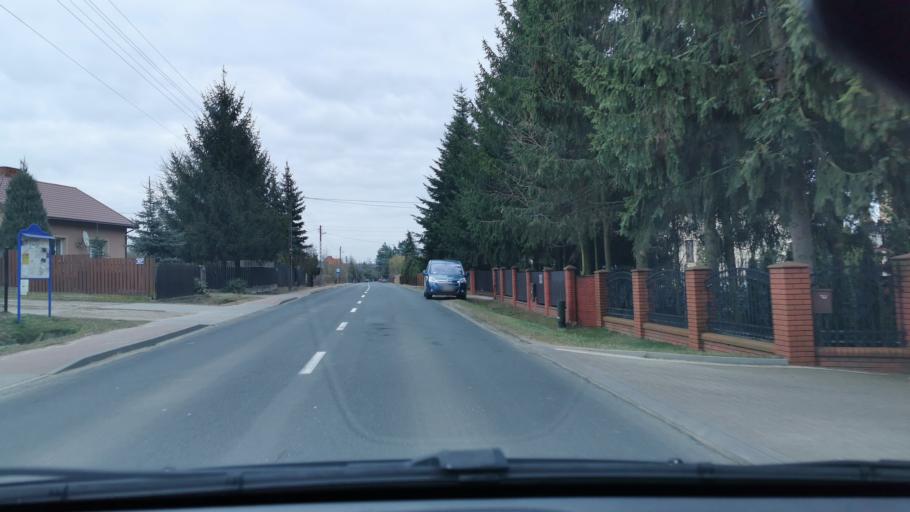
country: PL
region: Masovian Voivodeship
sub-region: Powiat zyrardowski
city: Radziejowice
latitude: 52.0097
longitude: 20.5396
